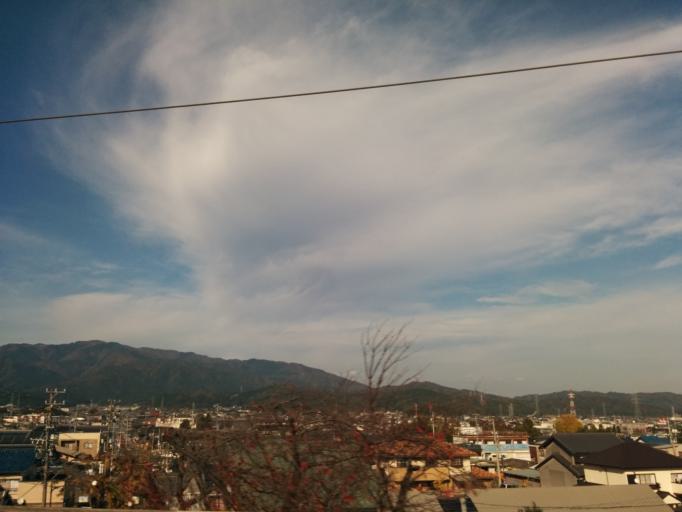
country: JP
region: Gifu
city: Tarui
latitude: 35.3660
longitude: 136.5272
